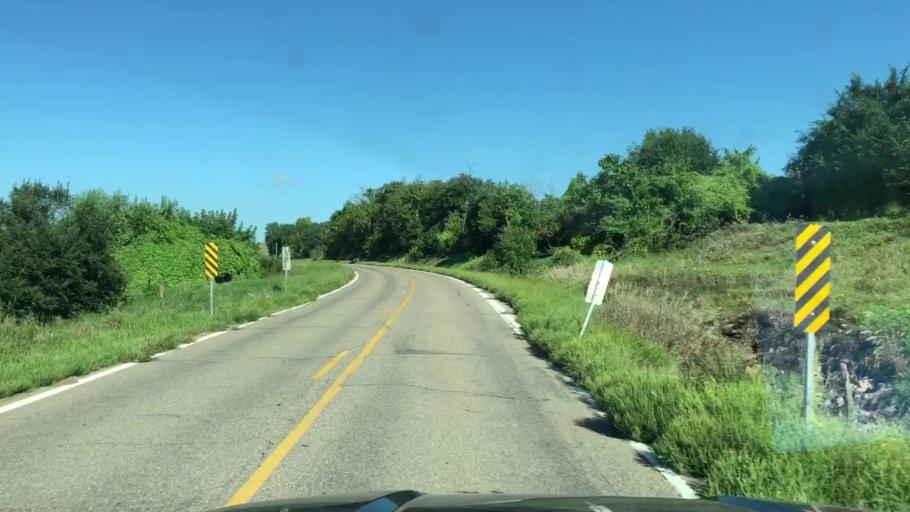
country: US
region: Iowa
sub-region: Woodbury County
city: Sergeant Bluff
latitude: 42.4198
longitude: -96.2677
